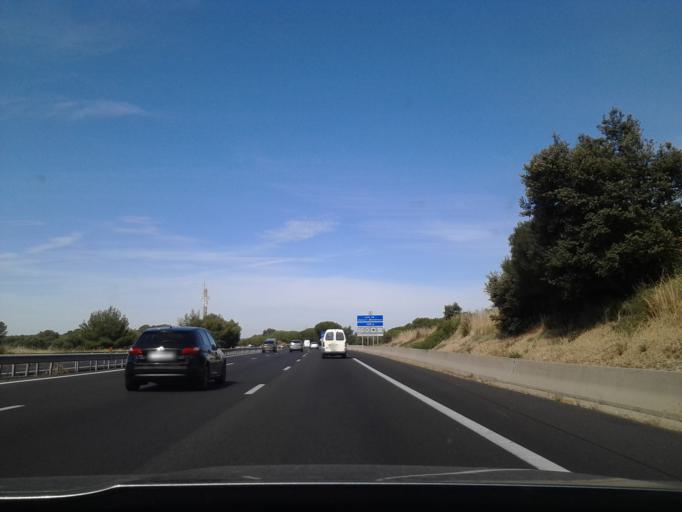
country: FR
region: Languedoc-Roussillon
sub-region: Departement de l'Herault
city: Montblanc
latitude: 43.3624
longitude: 3.3578
